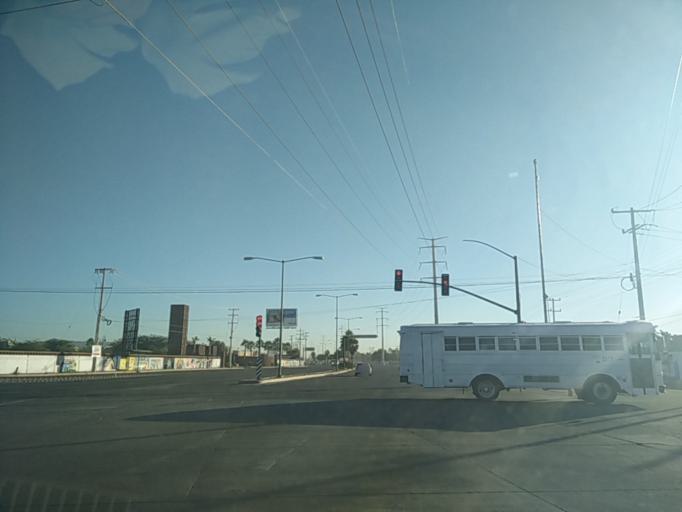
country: MX
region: Sonora
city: Hermosillo
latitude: 29.0824
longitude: -111.0062
